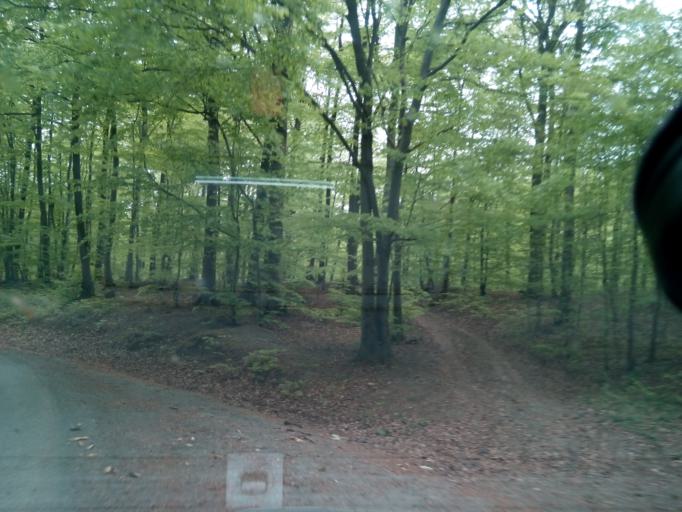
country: SK
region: Kosicky
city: Secovce
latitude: 48.8084
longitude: 21.5145
